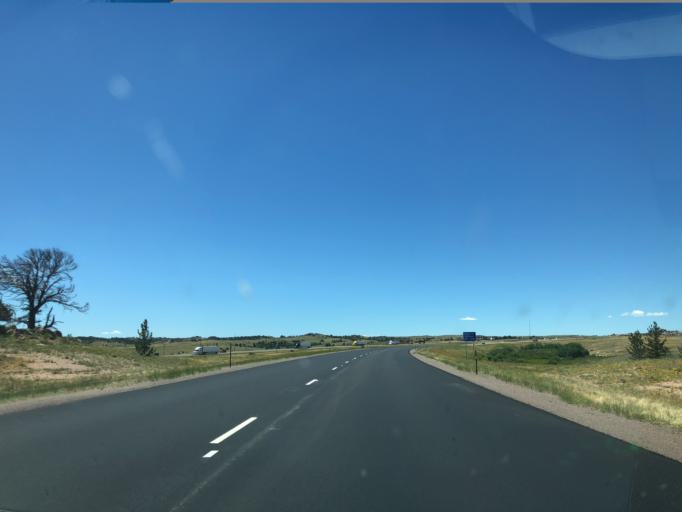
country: US
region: Wyoming
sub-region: Albany County
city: Laramie
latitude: 41.1281
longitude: -105.3344
